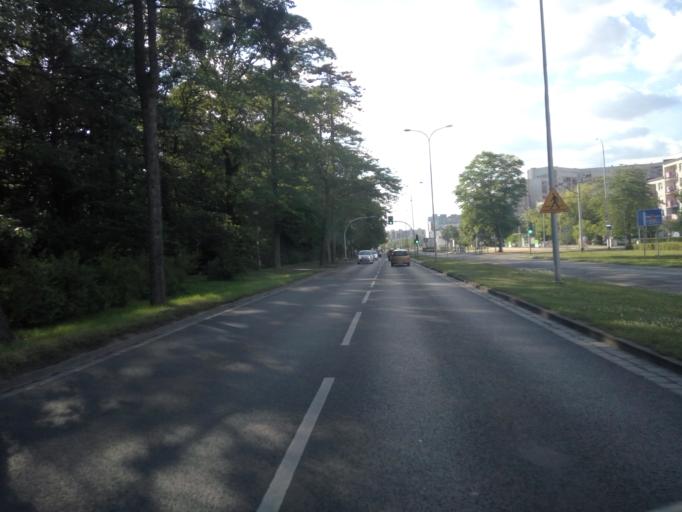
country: PL
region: Lower Silesian Voivodeship
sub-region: Powiat wroclawski
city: Wroclaw
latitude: 51.1344
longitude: 16.9701
